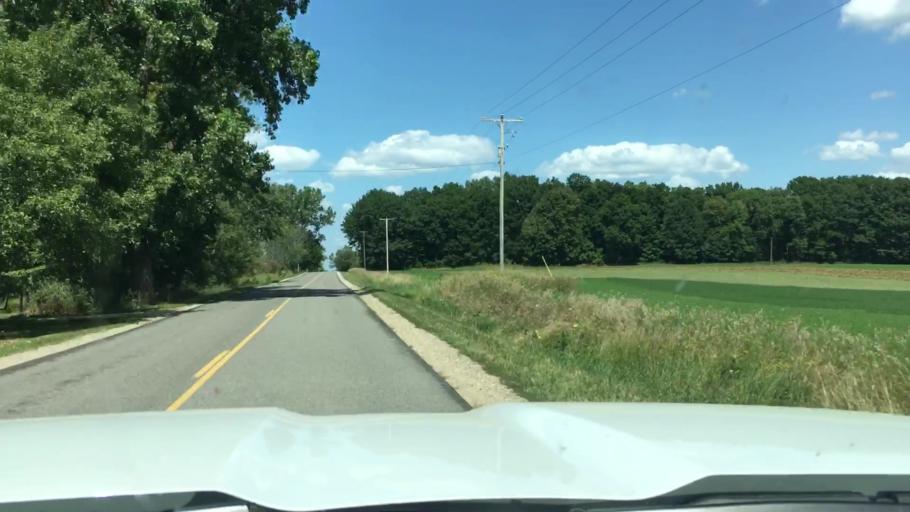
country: US
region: Michigan
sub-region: Muskegon County
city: Ravenna
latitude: 43.2540
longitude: -85.9180
